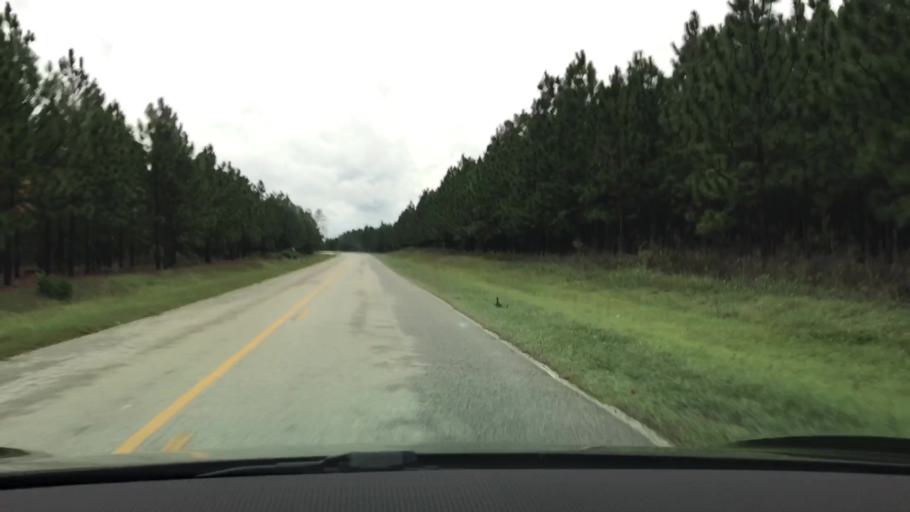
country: US
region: Georgia
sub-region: Jefferson County
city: Wadley
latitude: 32.8367
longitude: -82.3903
